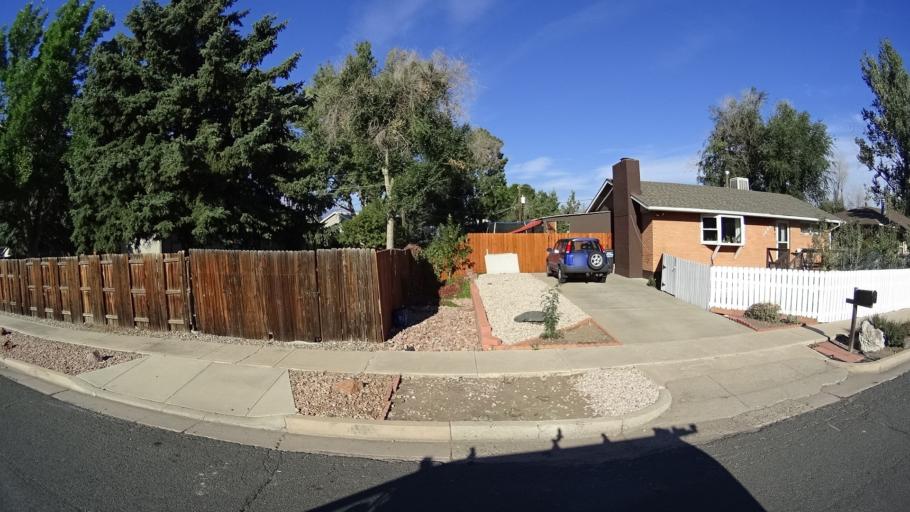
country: US
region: Colorado
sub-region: El Paso County
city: Cimarron Hills
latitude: 38.8921
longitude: -104.7666
